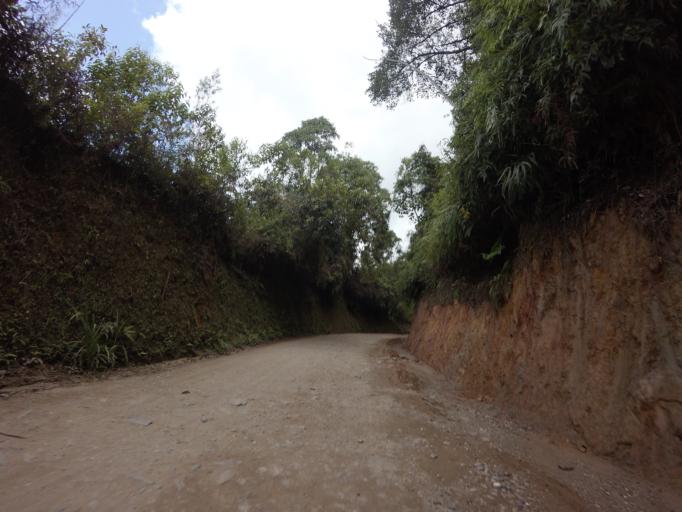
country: CO
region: Caldas
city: Victoria
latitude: 5.3064
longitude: -74.9790
